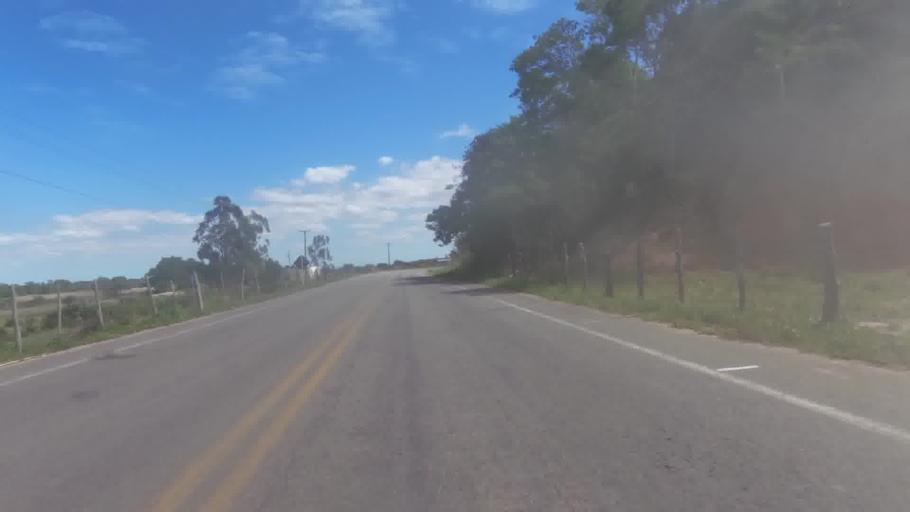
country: BR
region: Espirito Santo
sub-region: Marataizes
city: Marataizes
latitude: -21.1991
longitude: -40.9524
